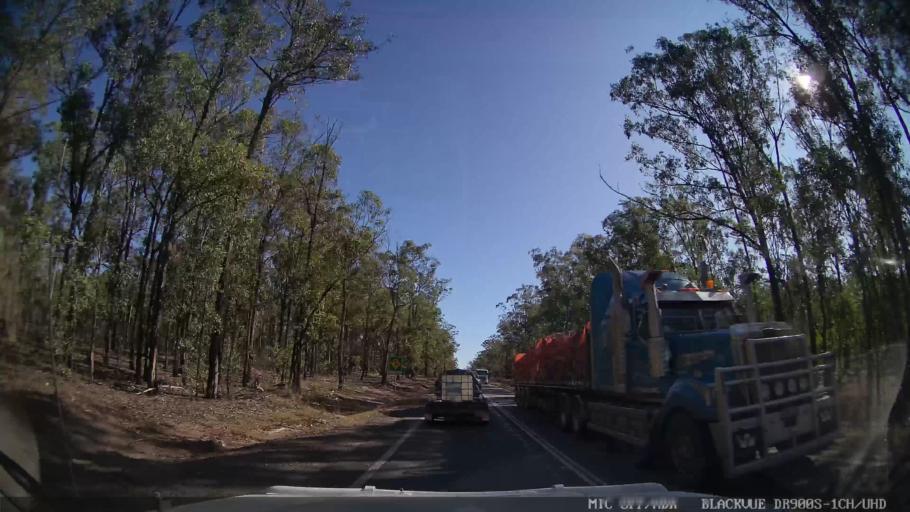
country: AU
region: Queensland
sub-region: Bundaberg
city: Childers
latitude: -25.2167
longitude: 152.0718
